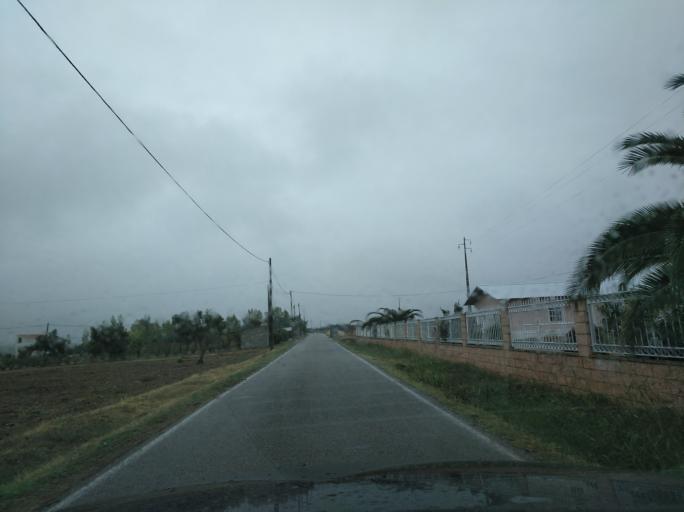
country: PT
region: Portalegre
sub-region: Campo Maior
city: Campo Maior
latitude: 38.9574
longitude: -7.0821
